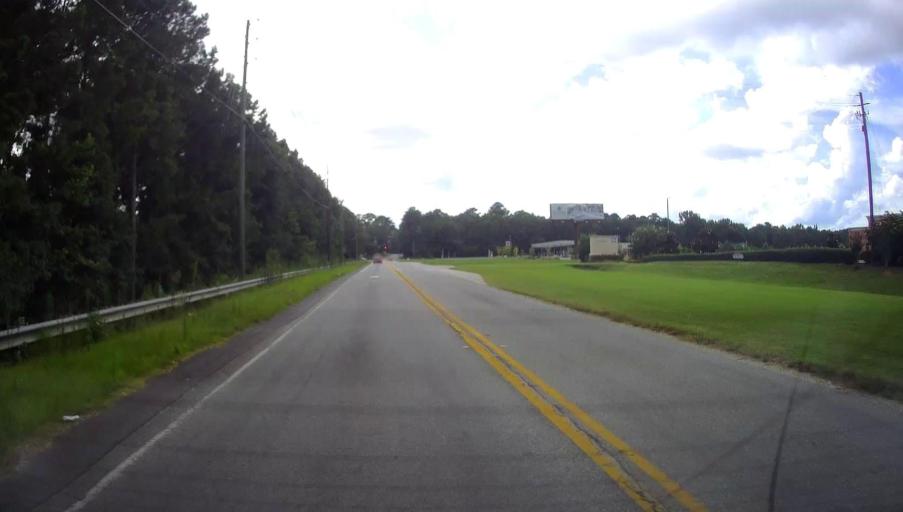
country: US
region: Alabama
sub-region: Russell County
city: Phenix City
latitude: 32.5645
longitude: -84.9464
